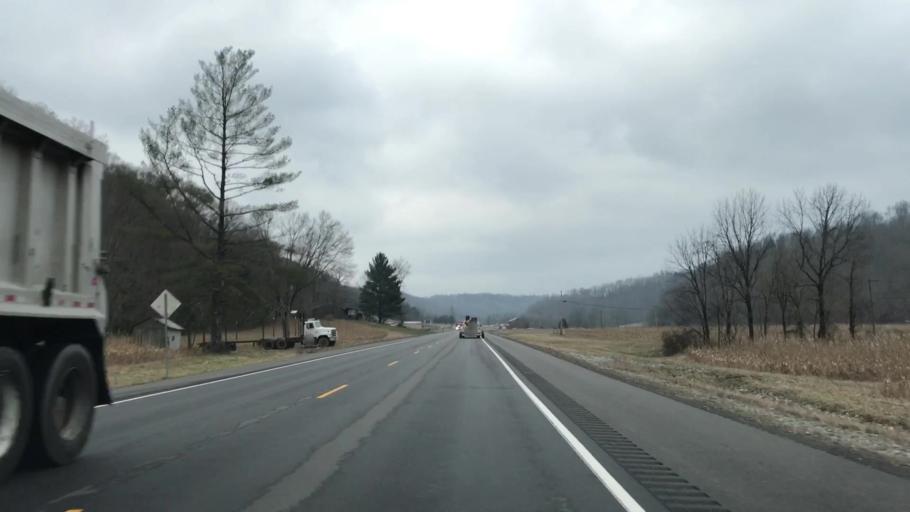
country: US
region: Kentucky
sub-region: Cumberland County
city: Burkesville
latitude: 36.8753
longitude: -85.3957
